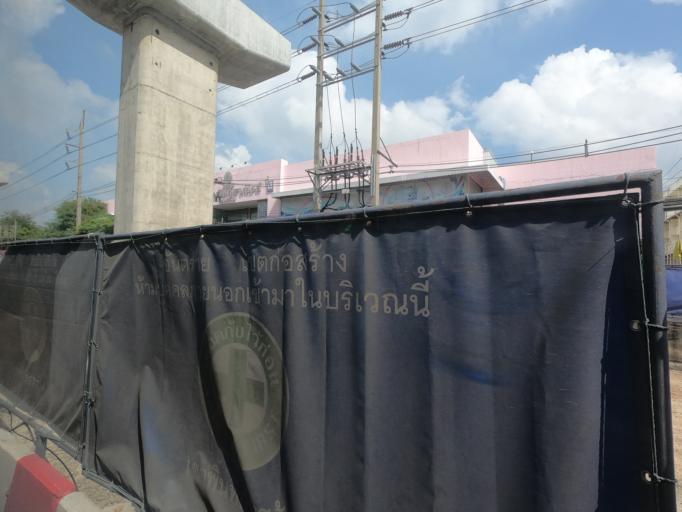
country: TH
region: Bangkok
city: Wang Thonglang
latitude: 13.7908
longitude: 100.6010
